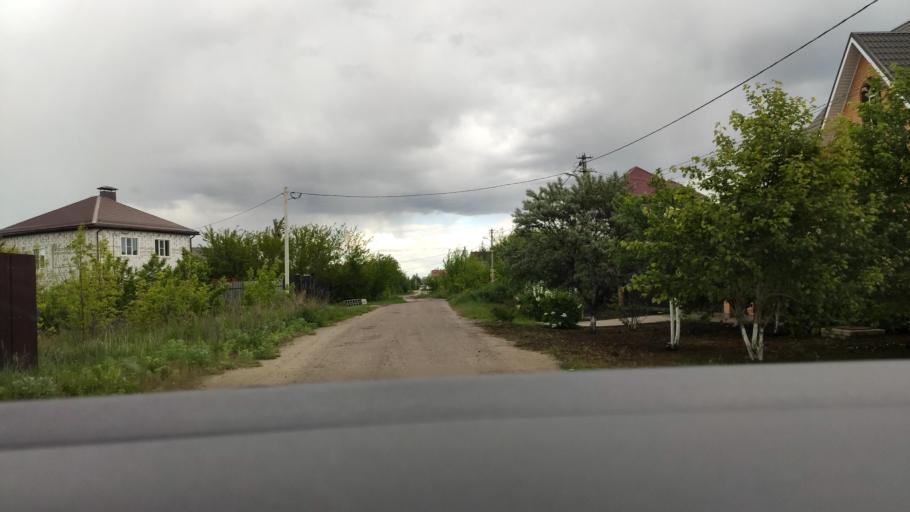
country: RU
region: Voronezj
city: Somovo
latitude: 51.6819
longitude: 39.3075
